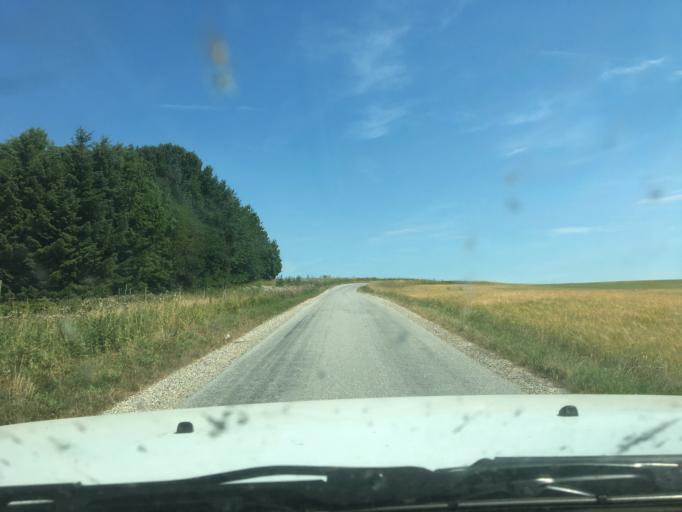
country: DK
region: Central Jutland
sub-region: Favrskov Kommune
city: Hadsten
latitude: 56.3945
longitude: 10.0674
